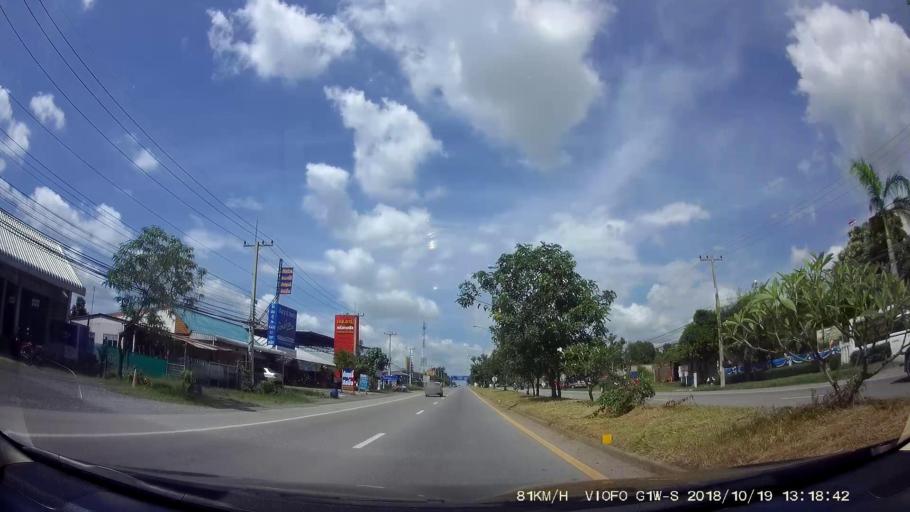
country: TH
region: Chaiyaphum
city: Chatturat
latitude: 15.4188
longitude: 101.8327
